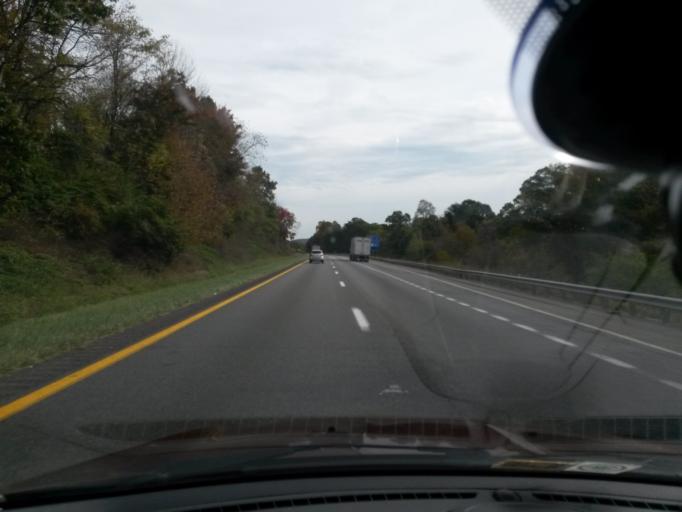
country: US
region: Virginia
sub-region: Botetourt County
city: Cloverdale
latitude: 37.3654
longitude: -79.9309
